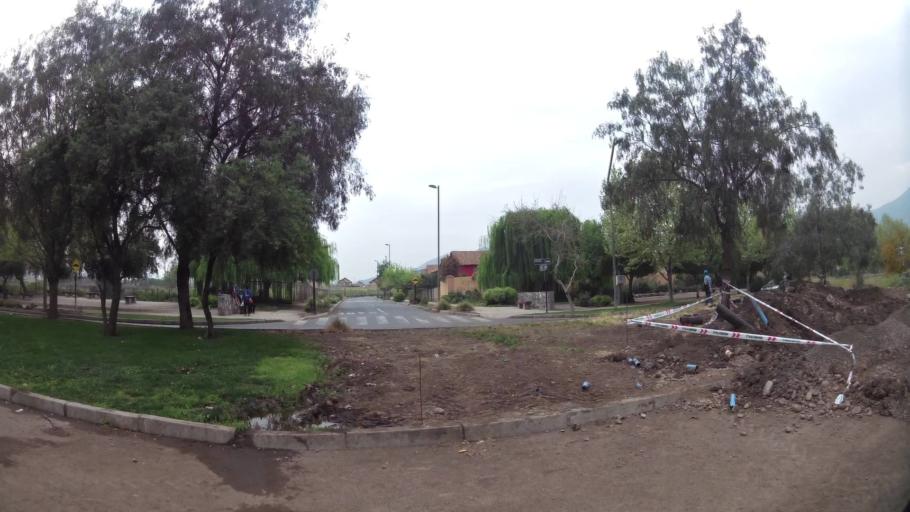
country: CL
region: Santiago Metropolitan
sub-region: Provincia de Chacabuco
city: Chicureo Abajo
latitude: -33.2019
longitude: -70.6534
